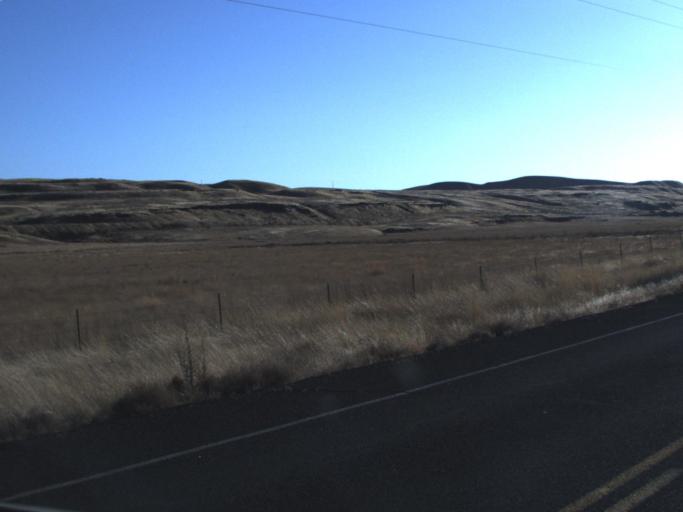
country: US
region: Washington
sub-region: Adams County
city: Ritzville
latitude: 46.7369
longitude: -118.3424
